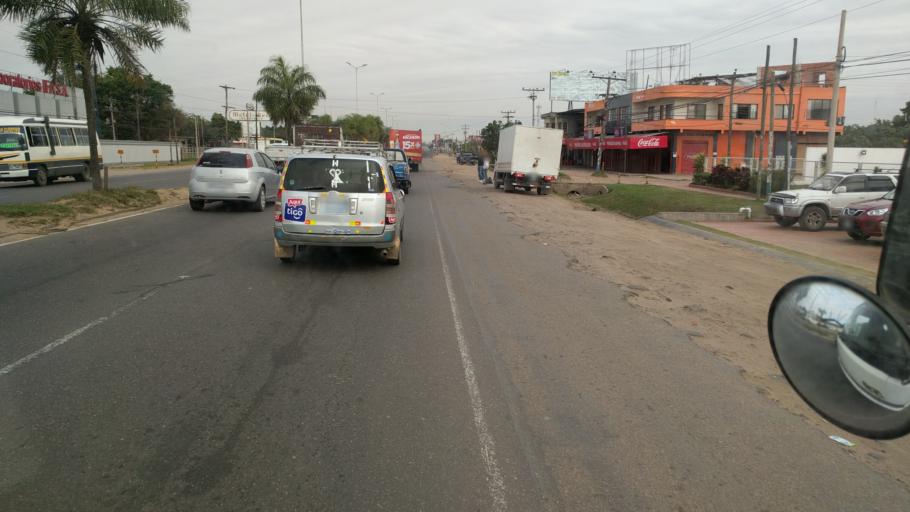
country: BO
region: Santa Cruz
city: Santa Cruz de la Sierra
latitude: -17.6971
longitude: -63.1596
